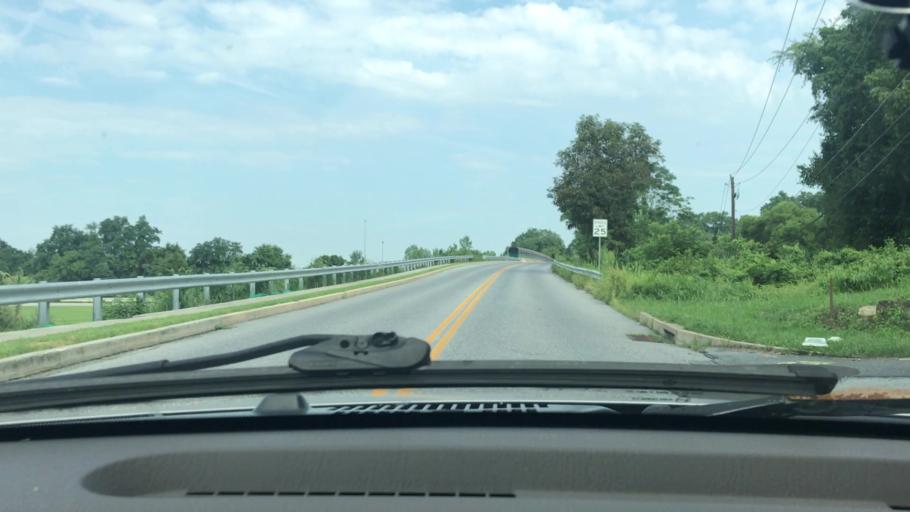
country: US
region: Pennsylvania
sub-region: Dauphin County
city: Middletown
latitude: 40.2027
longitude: -76.7562
